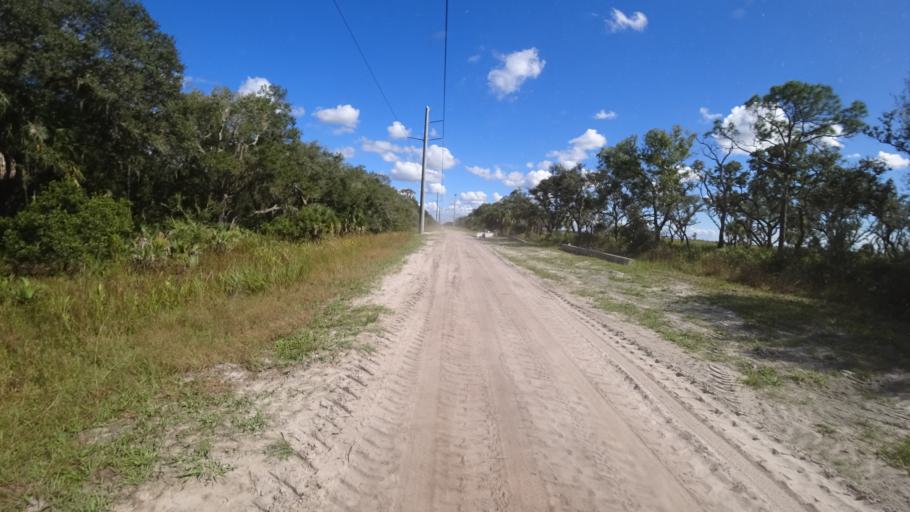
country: US
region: Florida
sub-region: Sarasota County
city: Lake Sarasota
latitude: 27.2457
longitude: -82.2759
